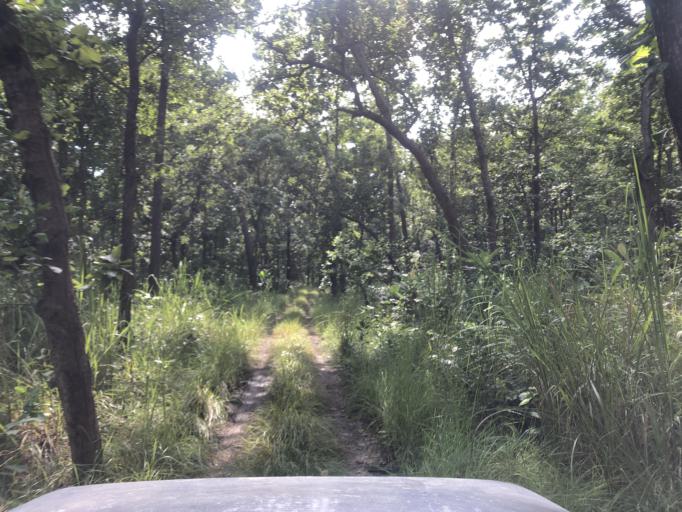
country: NP
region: Far Western
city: Tikapur
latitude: 28.5601
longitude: 81.2949
